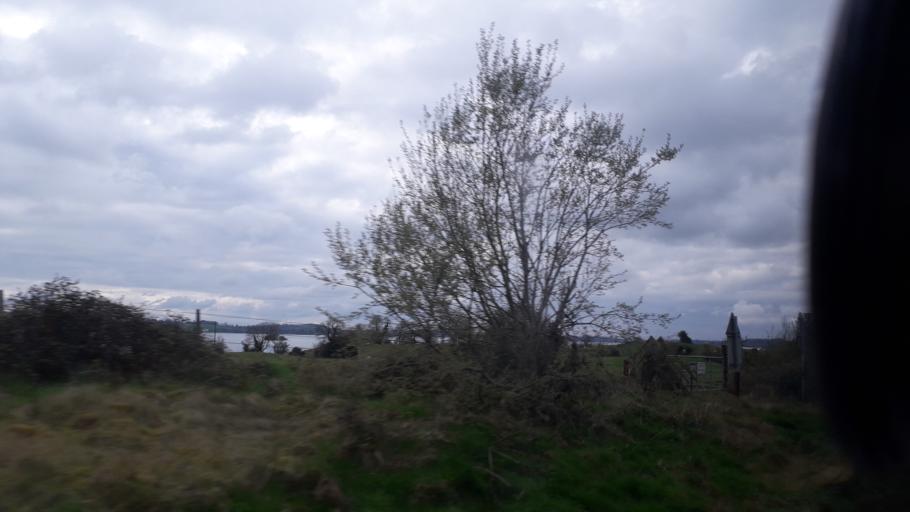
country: IE
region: Leinster
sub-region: An Iarmhi
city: An Muileann gCearr
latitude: 53.5577
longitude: -7.3625
